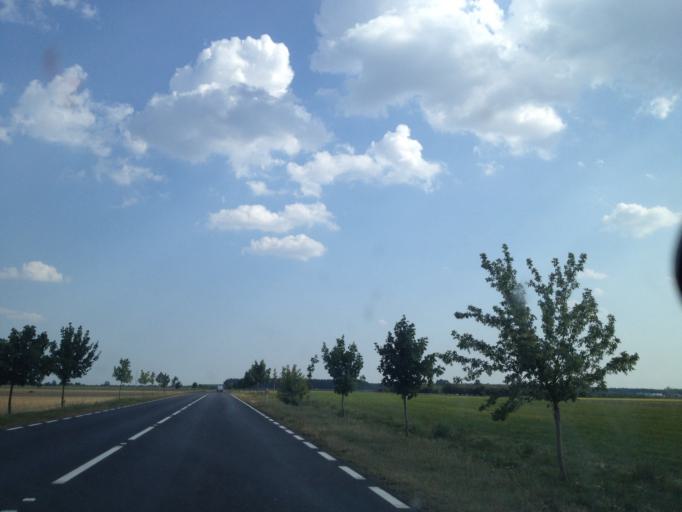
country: PL
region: Greater Poland Voivodeship
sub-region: Powiat poznanski
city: Kornik
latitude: 52.2348
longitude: 17.0619
